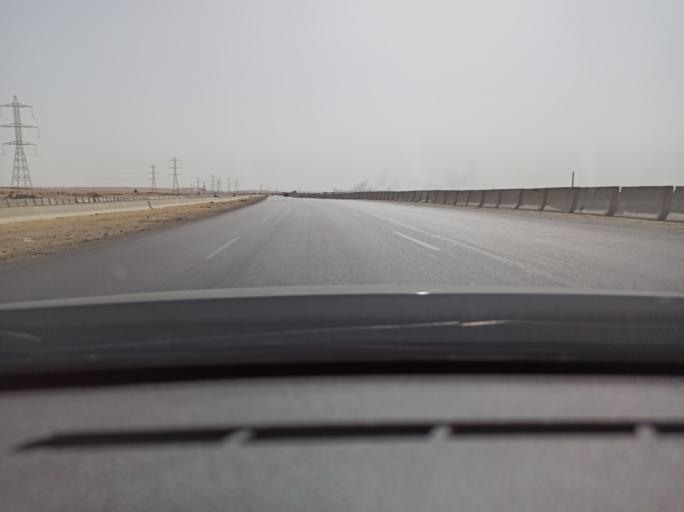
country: EG
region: Muhafazat al Qahirah
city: Halwan
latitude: 29.7716
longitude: 31.3737
